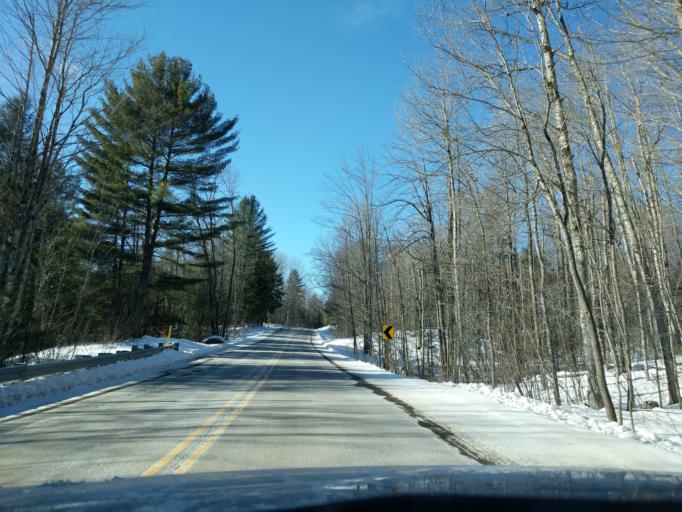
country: US
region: Wisconsin
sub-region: Menominee County
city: Keshena
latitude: 45.1130
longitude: -88.6433
